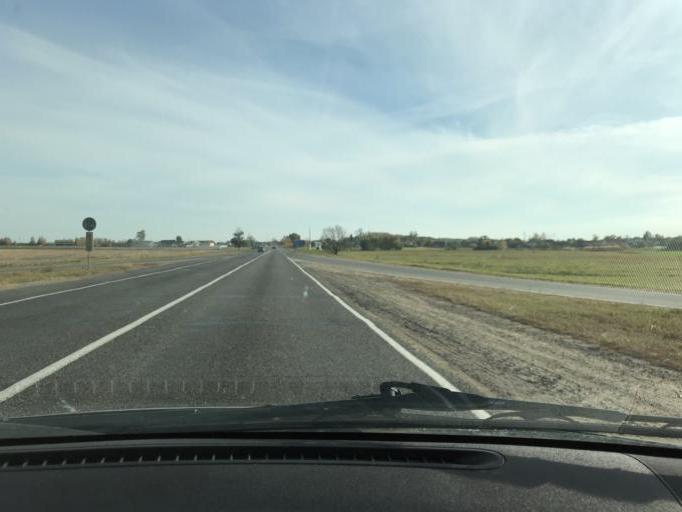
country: BY
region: Brest
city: Asnyezhytsy
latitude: 52.1824
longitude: 26.0822
